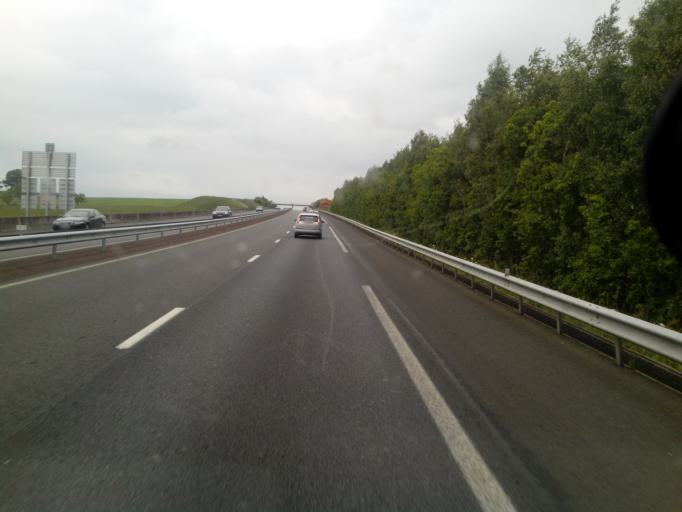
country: FR
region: Lower Normandy
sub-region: Departement de la Manche
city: Ducey
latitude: 48.5970
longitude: -1.3299
